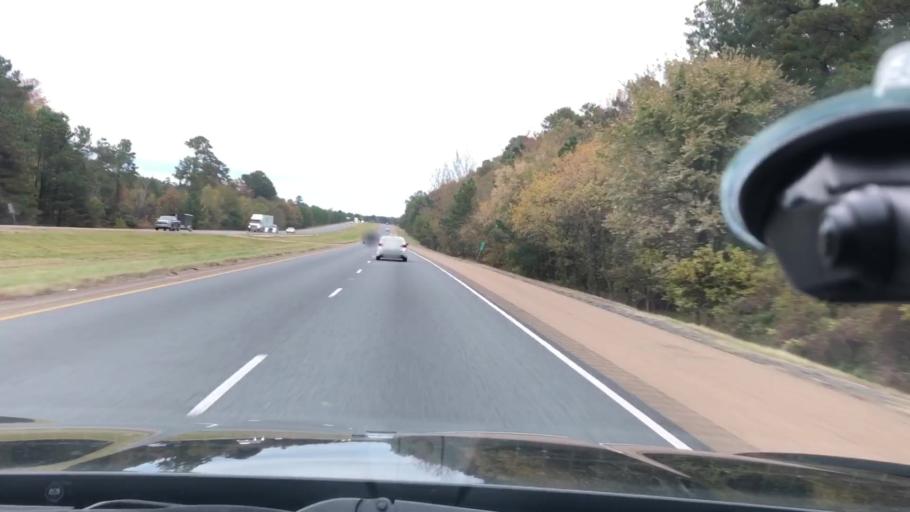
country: US
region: Arkansas
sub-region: Clark County
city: Gurdon
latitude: 33.9448
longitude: -93.2402
